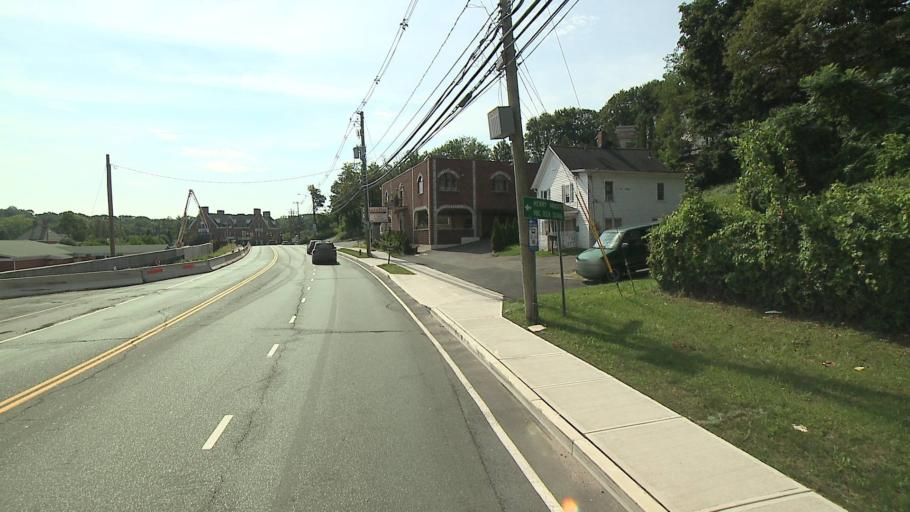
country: US
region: Connecticut
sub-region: Fairfield County
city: Danbury
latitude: 41.4126
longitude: -73.4575
